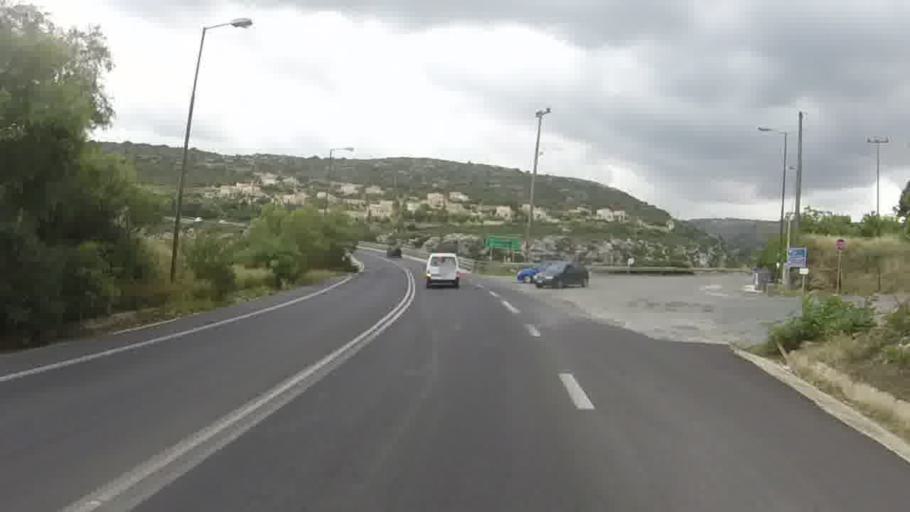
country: GR
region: Crete
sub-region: Nomos Rethymnis
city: Atsipopoulon
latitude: 35.3598
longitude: 24.4060
